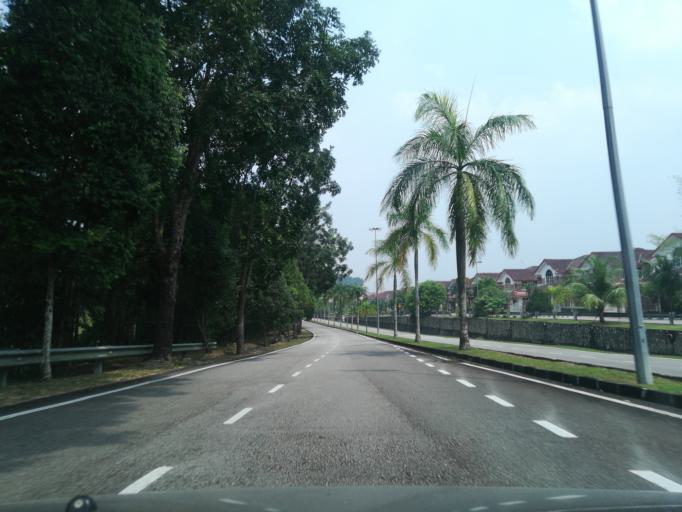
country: MY
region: Kedah
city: Kulim
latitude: 5.3957
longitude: 100.5808
